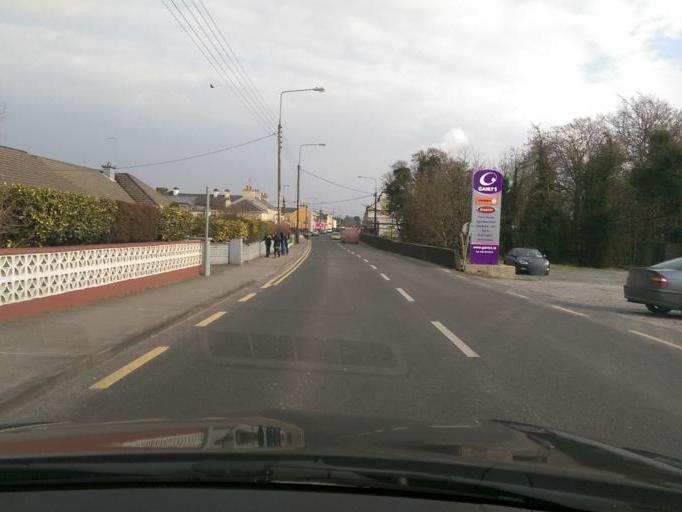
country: IE
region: Connaught
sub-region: County Galway
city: Loughrea
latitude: 53.4705
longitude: -8.5030
